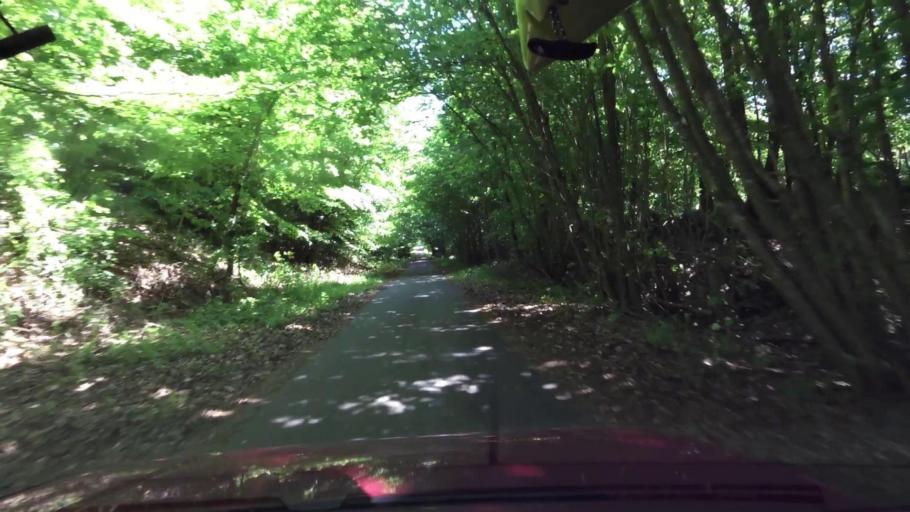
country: PL
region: West Pomeranian Voivodeship
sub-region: Powiat koszalinski
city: Polanow
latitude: 54.0348
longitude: 16.7921
